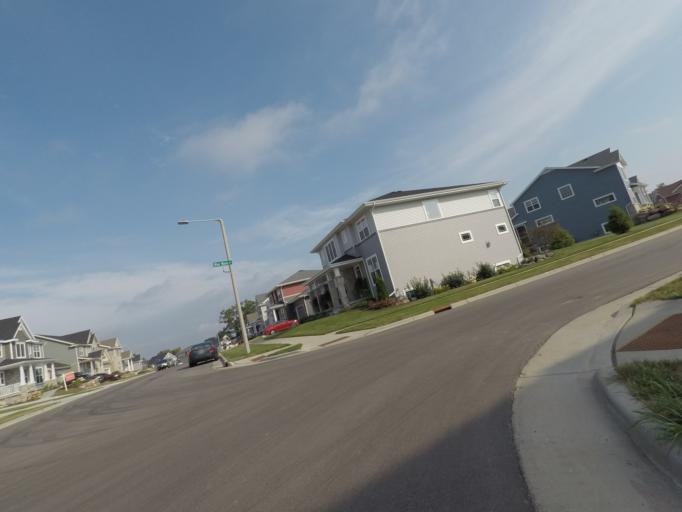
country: US
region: Wisconsin
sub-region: Dane County
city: Verona
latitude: 43.0540
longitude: -89.5645
